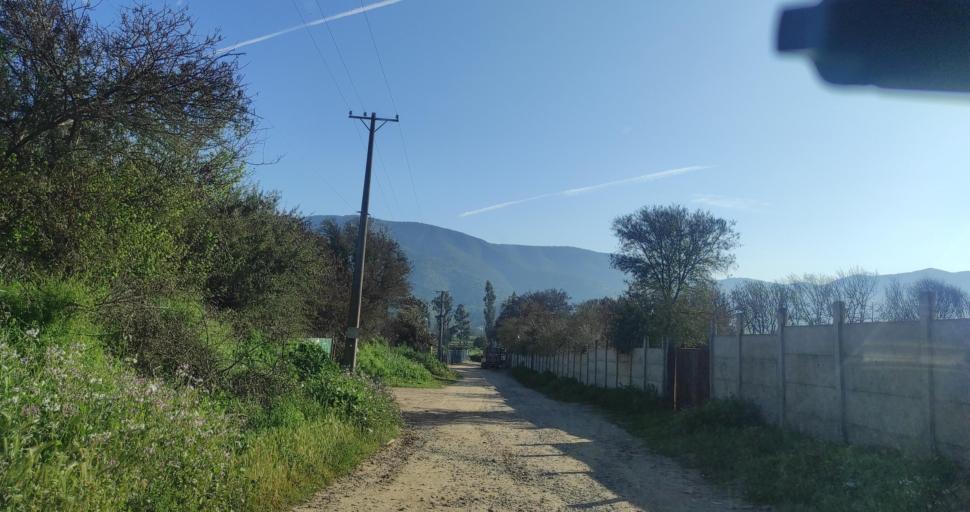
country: CL
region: Valparaiso
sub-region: Provincia de Marga Marga
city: Limache
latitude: -33.0019
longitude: -71.2534
